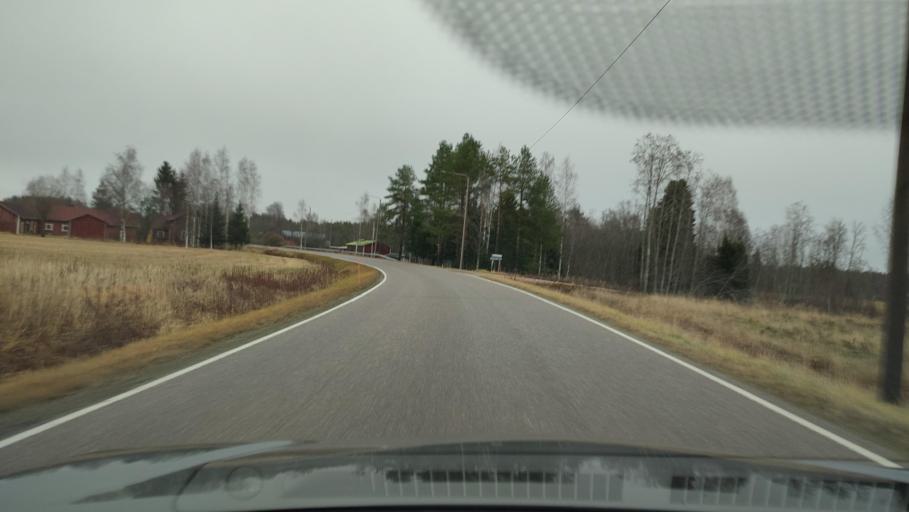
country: FI
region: Southern Ostrobothnia
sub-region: Suupohja
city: Isojoki
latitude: 62.2361
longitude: 22.0278
